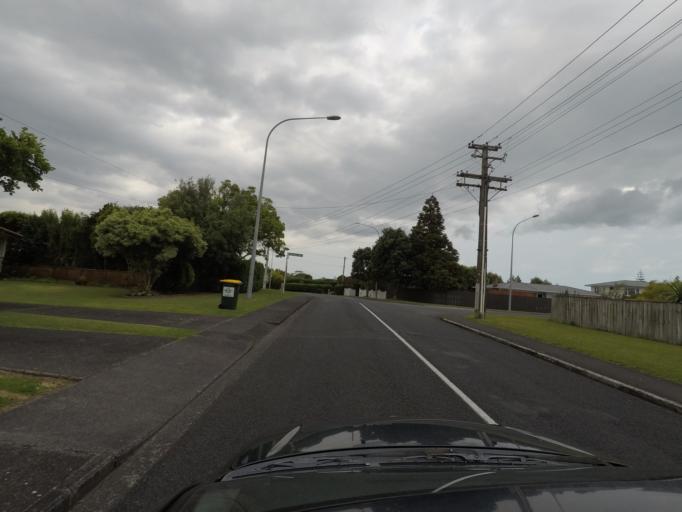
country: NZ
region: Auckland
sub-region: Auckland
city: Rosebank
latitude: -36.8469
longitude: 174.6467
